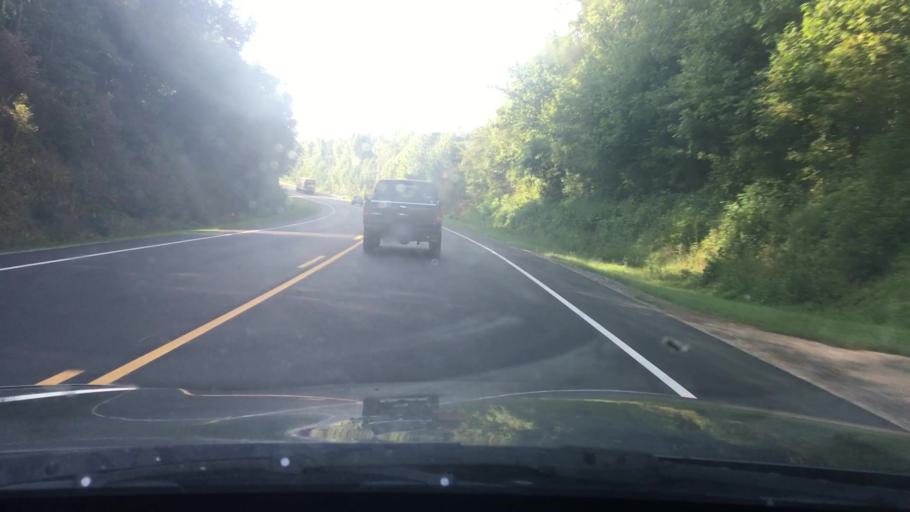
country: US
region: North Carolina
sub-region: Caswell County
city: Yanceyville
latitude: 36.4249
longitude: -79.3565
